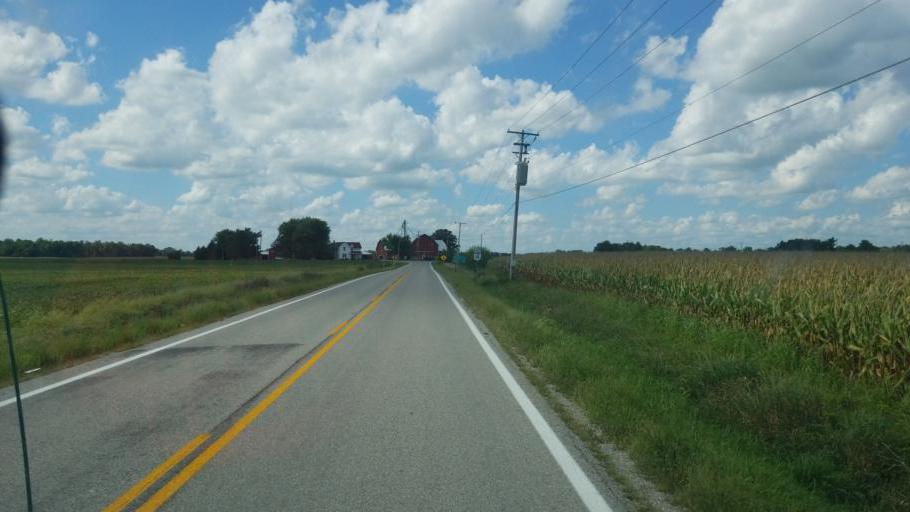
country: US
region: Ohio
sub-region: Union County
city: Richwood
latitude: 40.3804
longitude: -83.2774
